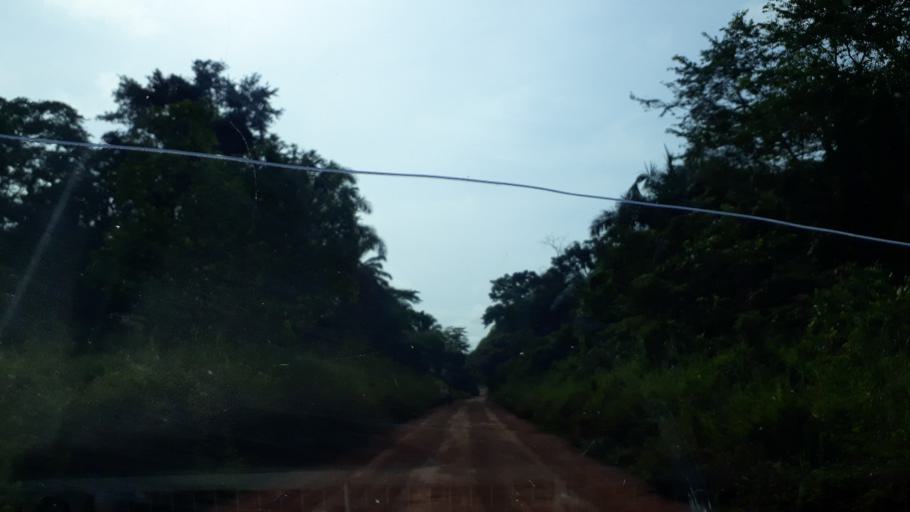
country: CD
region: Eastern Province
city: Wamba
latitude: 1.4005
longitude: 27.6655
